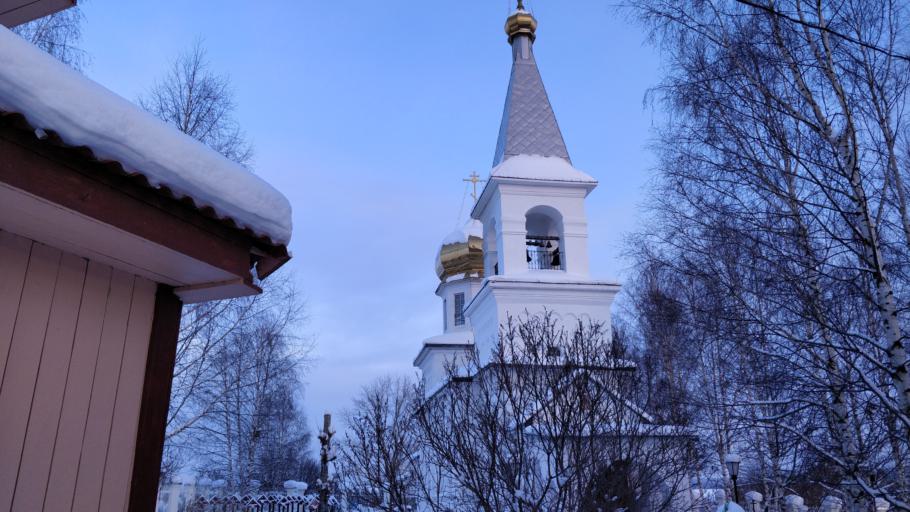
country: RU
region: Perm
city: Verkhnechusovskiye Gorodki
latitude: 58.1978
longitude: 57.1386
